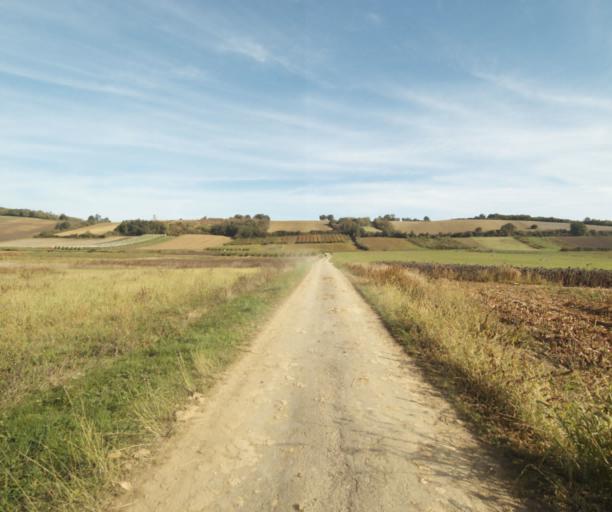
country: FR
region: Midi-Pyrenees
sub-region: Departement du Tarn-et-Garonne
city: Orgueil
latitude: 43.9200
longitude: 1.4337
